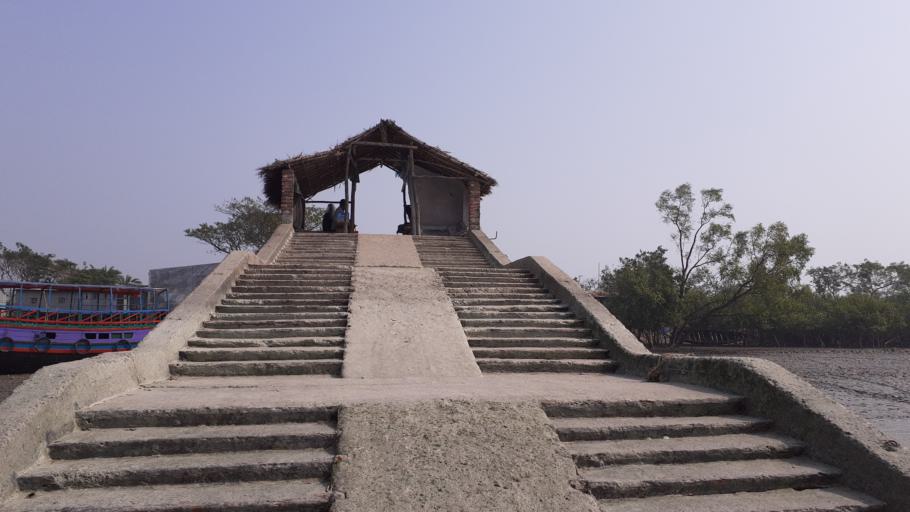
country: IN
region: West Bengal
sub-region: North 24 Parganas
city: Gosaba
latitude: 22.2461
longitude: 89.2489
